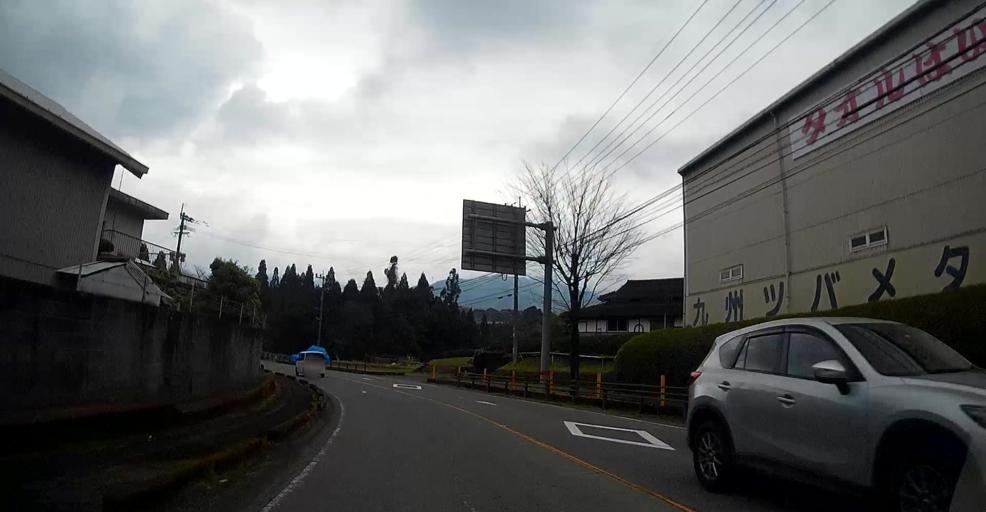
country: JP
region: Kumamoto
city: Matsubase
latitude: 32.6233
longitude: 130.8150
